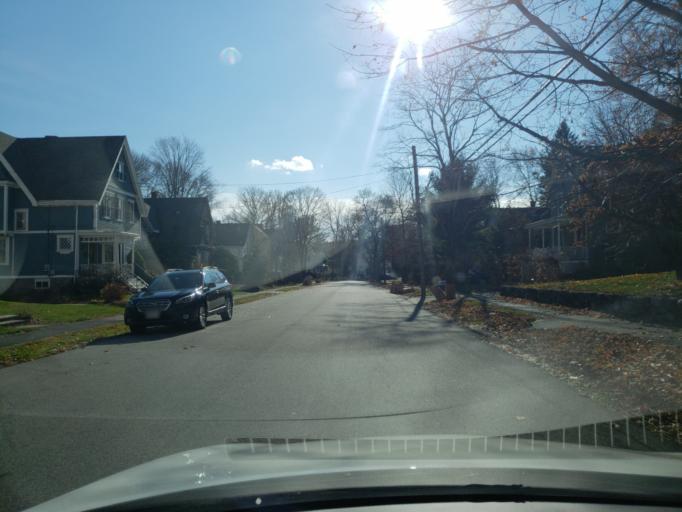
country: US
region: Massachusetts
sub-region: Essex County
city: Andover
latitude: 42.6600
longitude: -71.1330
